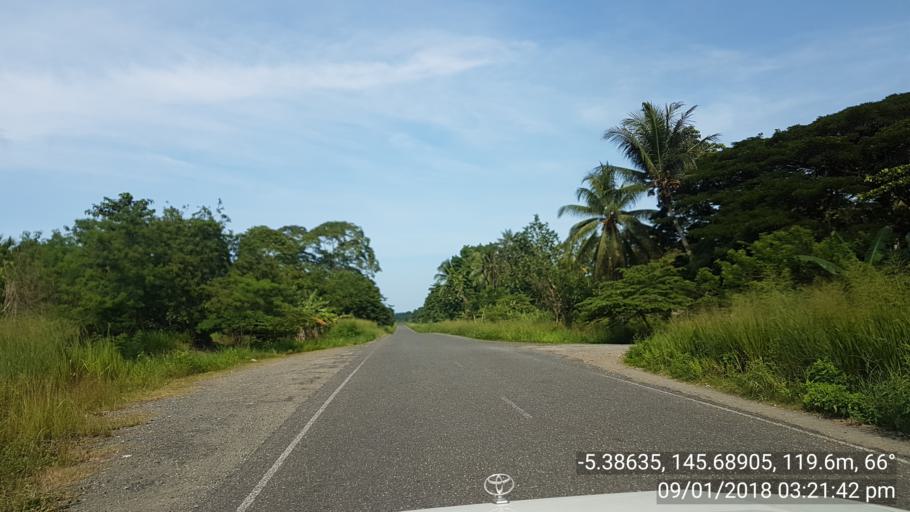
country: PG
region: Madang
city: Madang
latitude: -5.3864
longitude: 145.6889
